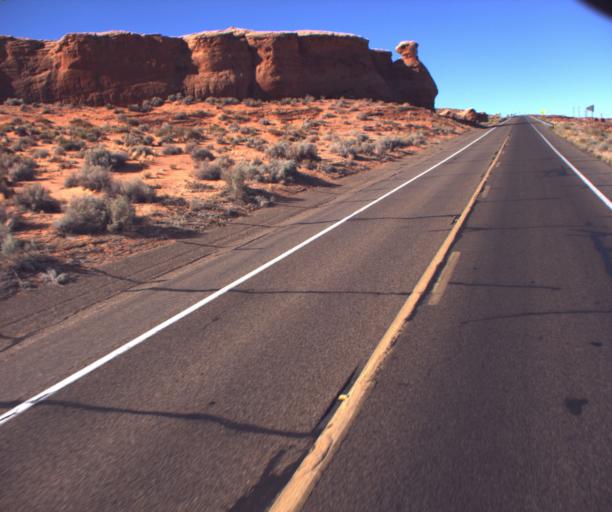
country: US
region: Arizona
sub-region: Coconino County
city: Page
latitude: 36.9433
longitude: -111.4957
